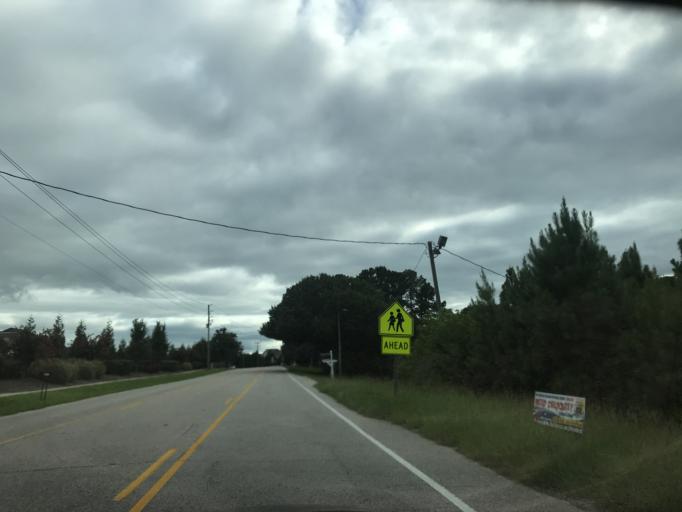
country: US
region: North Carolina
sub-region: Johnston County
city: Clayton
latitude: 35.5784
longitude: -78.5449
